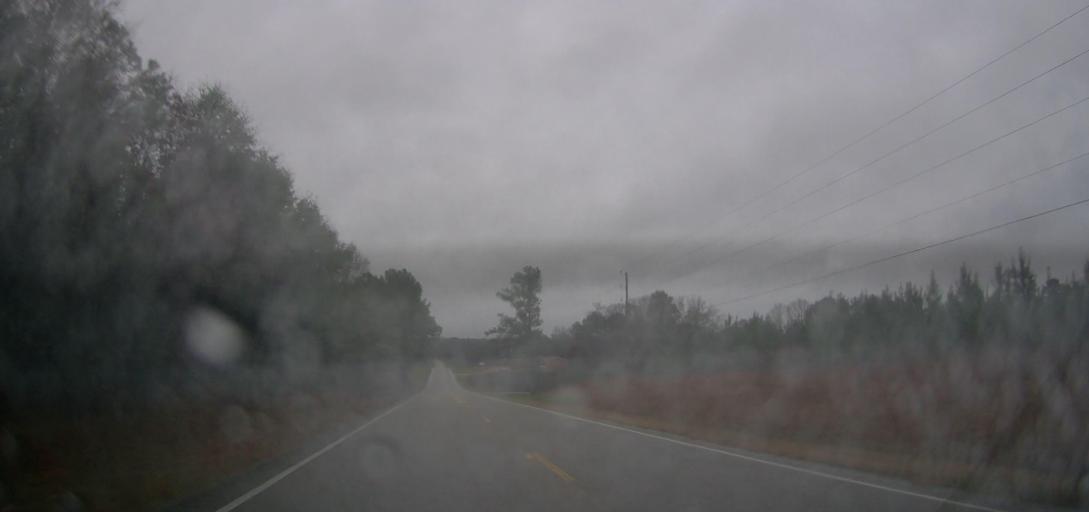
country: US
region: Alabama
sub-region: Autauga County
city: Pine Level
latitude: 32.5405
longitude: -86.6430
